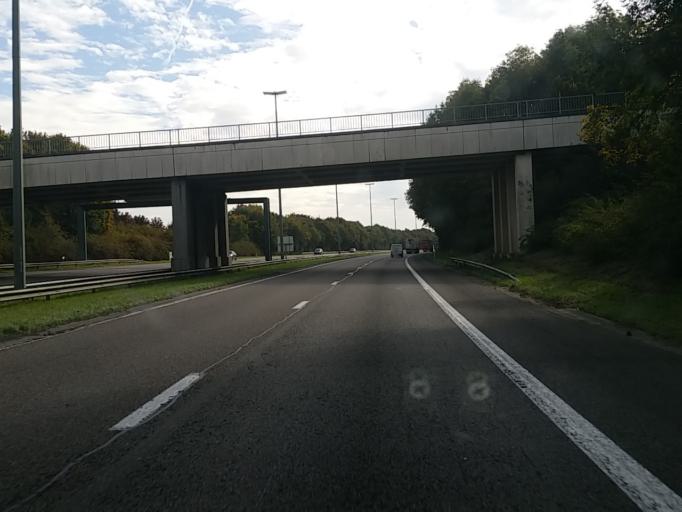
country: BE
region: Wallonia
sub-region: Province du Luxembourg
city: Arlon
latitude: 49.6685
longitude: 5.7978
